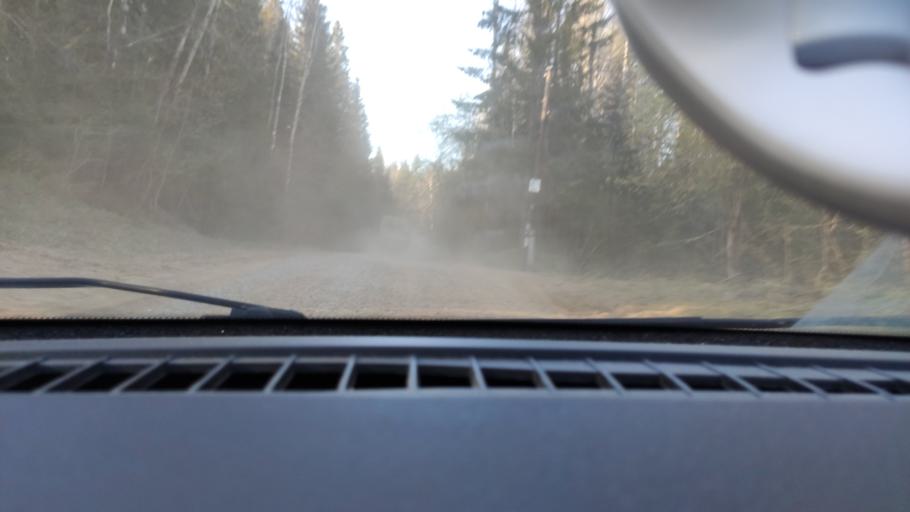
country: RU
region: Perm
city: Novyye Lyady
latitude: 58.1239
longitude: 56.4576
